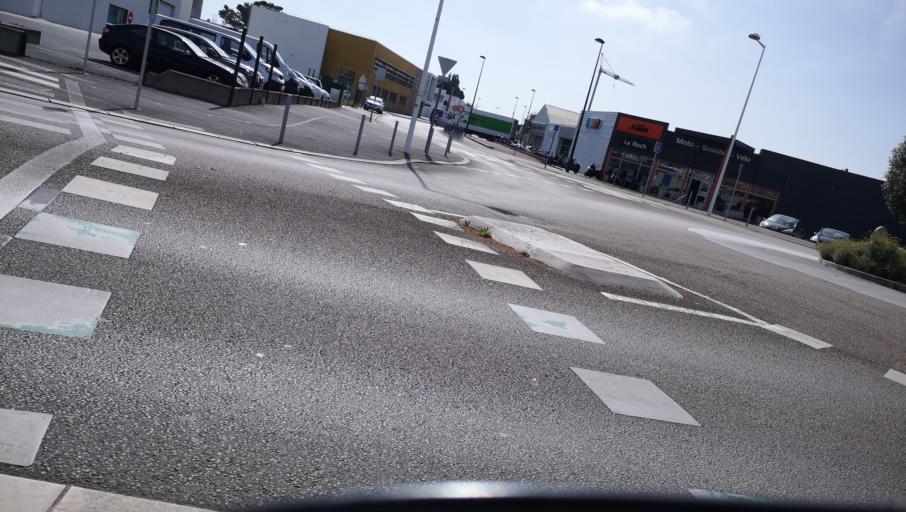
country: FR
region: Pays de la Loire
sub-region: Departement de la Vendee
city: Les Sables-d'Olonne
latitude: 46.5125
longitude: -1.7767
